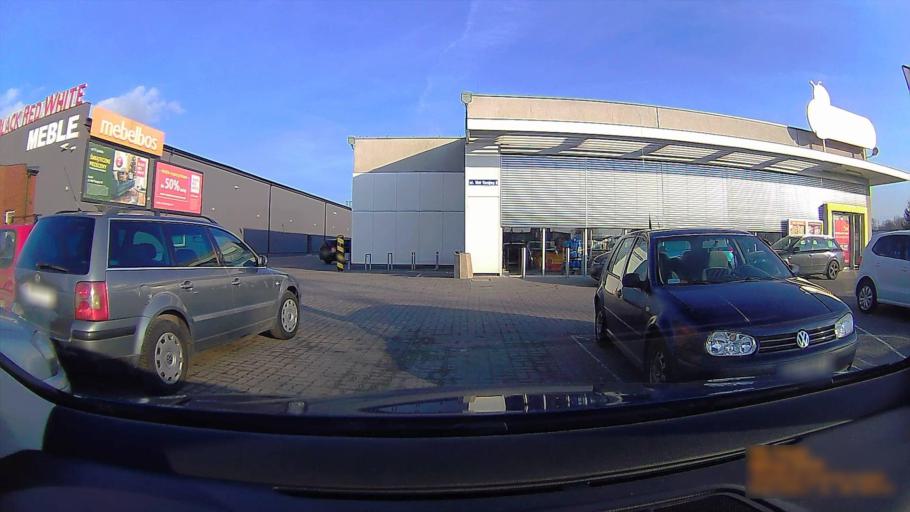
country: PL
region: Greater Poland Voivodeship
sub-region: Konin
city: Konin
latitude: 52.2183
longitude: 18.2852
